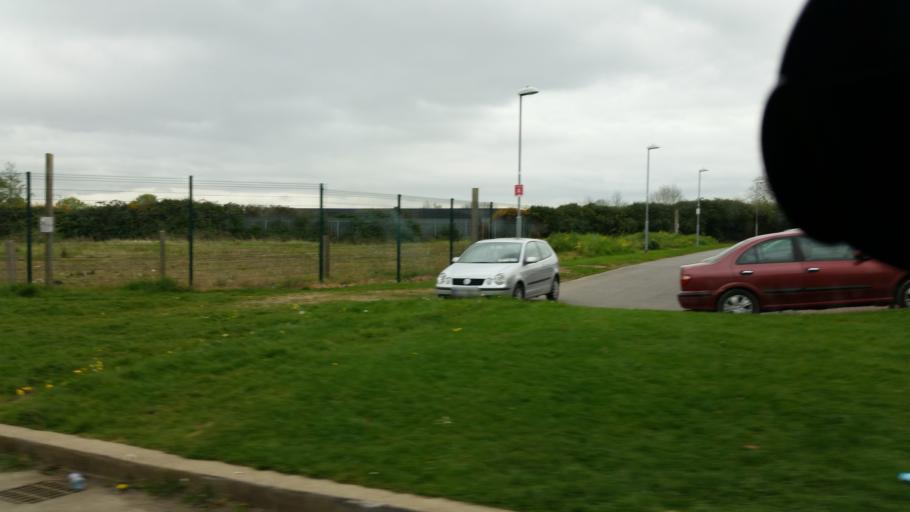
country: IE
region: Leinster
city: Ballymun
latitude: 53.4042
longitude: -6.2831
